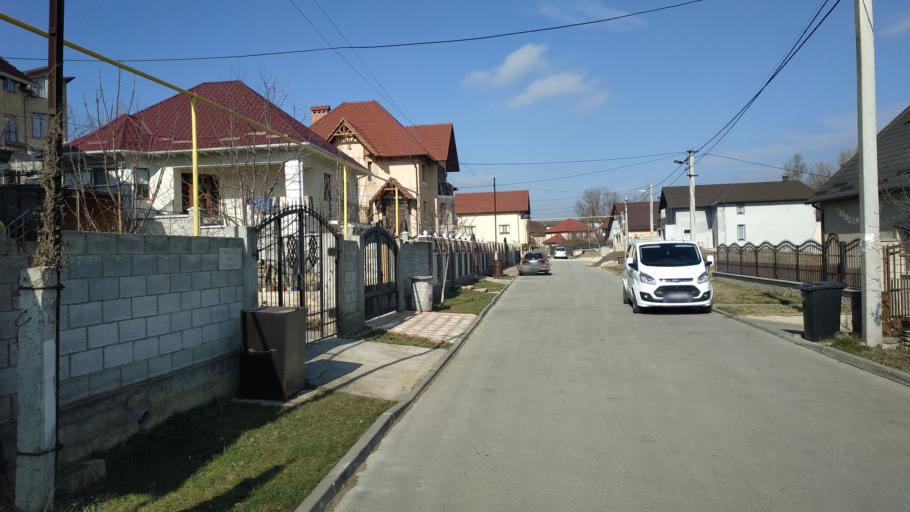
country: MD
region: Chisinau
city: Vatra
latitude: 47.0348
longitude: 28.7608
